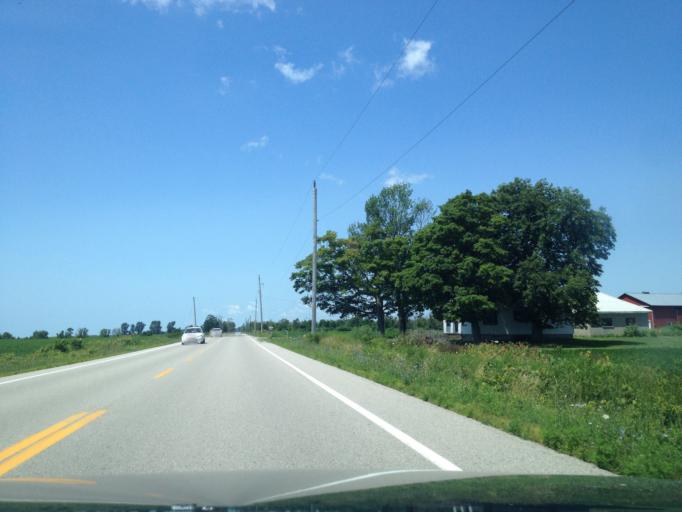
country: CA
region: Ontario
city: Norfolk County
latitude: 42.5771
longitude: -80.5514
